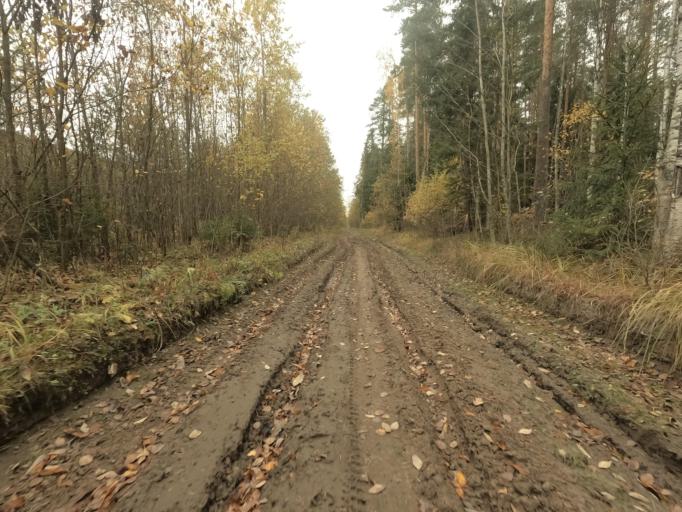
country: RU
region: Leningrad
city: Pavlovo
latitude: 59.7751
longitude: 30.9030
